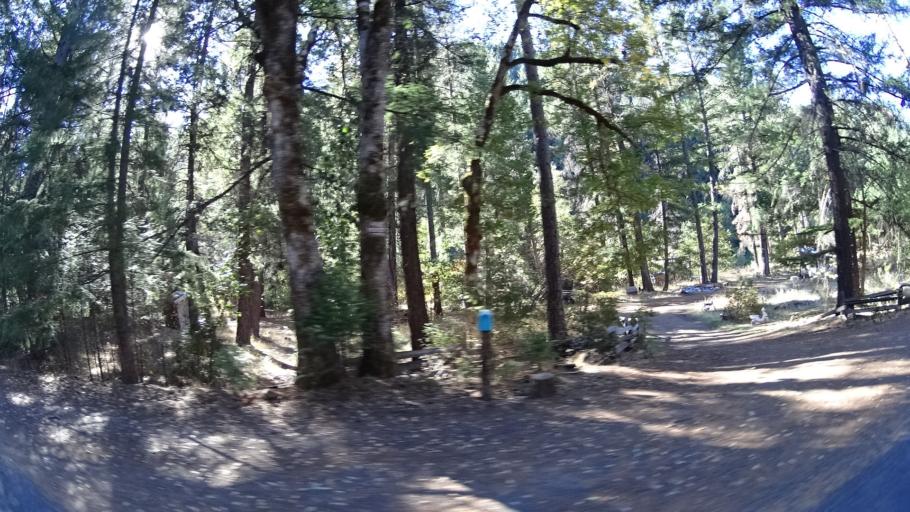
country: US
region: California
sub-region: Trinity County
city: Weaverville
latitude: 41.1426
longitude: -123.1648
